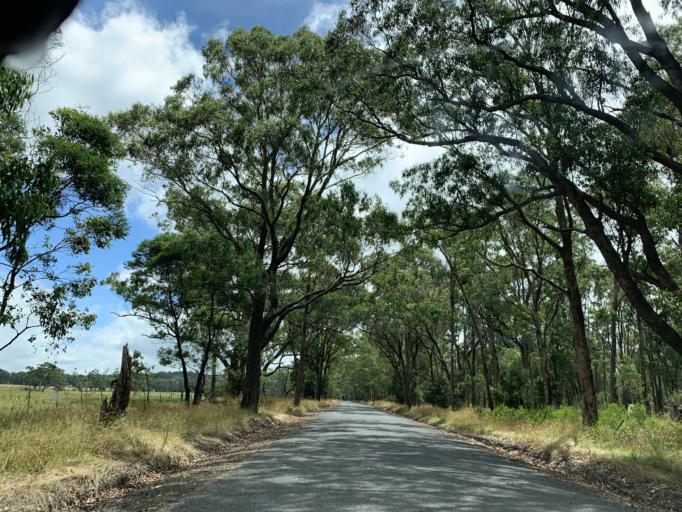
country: AU
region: Victoria
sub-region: Latrobe
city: Traralgon
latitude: -38.1134
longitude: 146.5517
